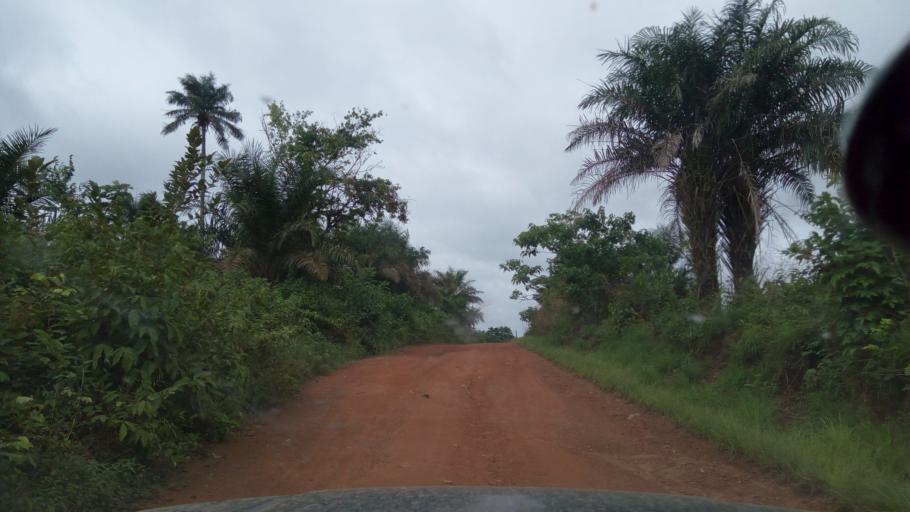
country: SL
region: Eastern Province
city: Kenema
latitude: 7.7805
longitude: -11.1805
